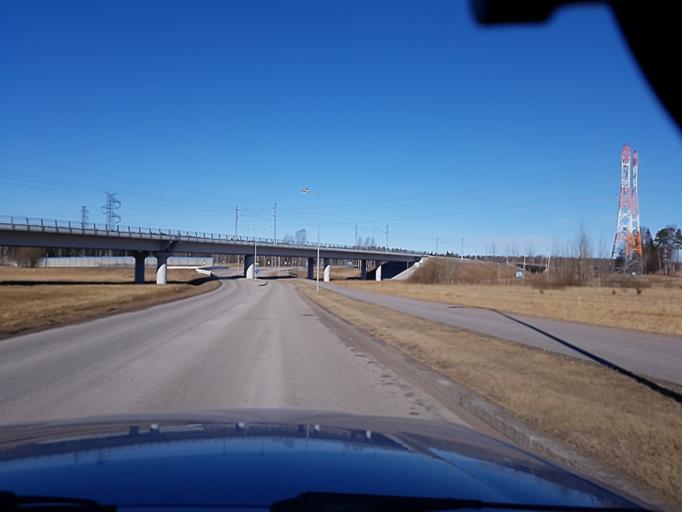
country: FI
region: Uusimaa
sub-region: Helsinki
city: Kilo
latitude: 60.2885
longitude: 24.8478
